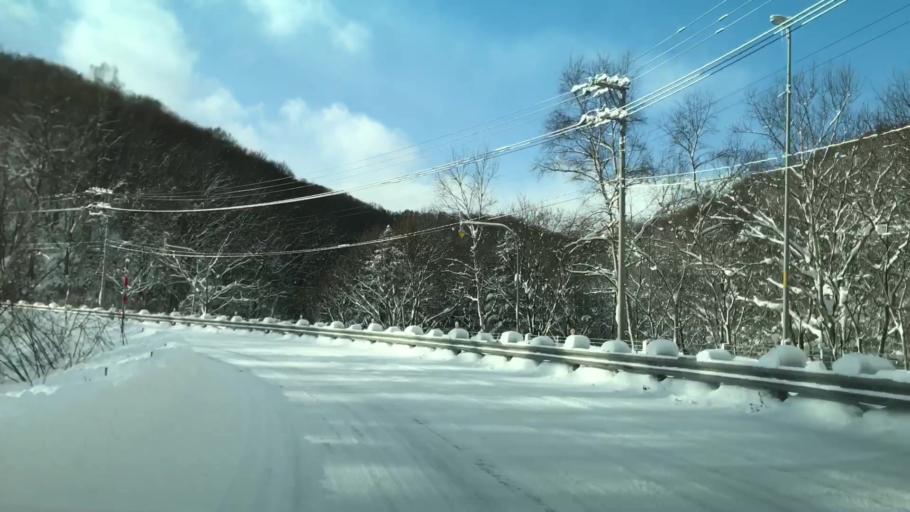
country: JP
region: Hokkaido
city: Yoichi
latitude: 43.2926
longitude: 140.5859
